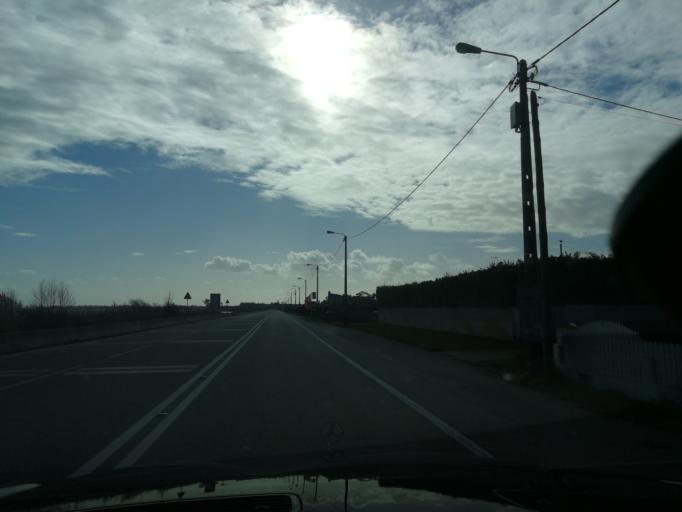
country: PT
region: Aveiro
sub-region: Estarreja
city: Pardilho
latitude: 40.7817
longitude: -8.6886
